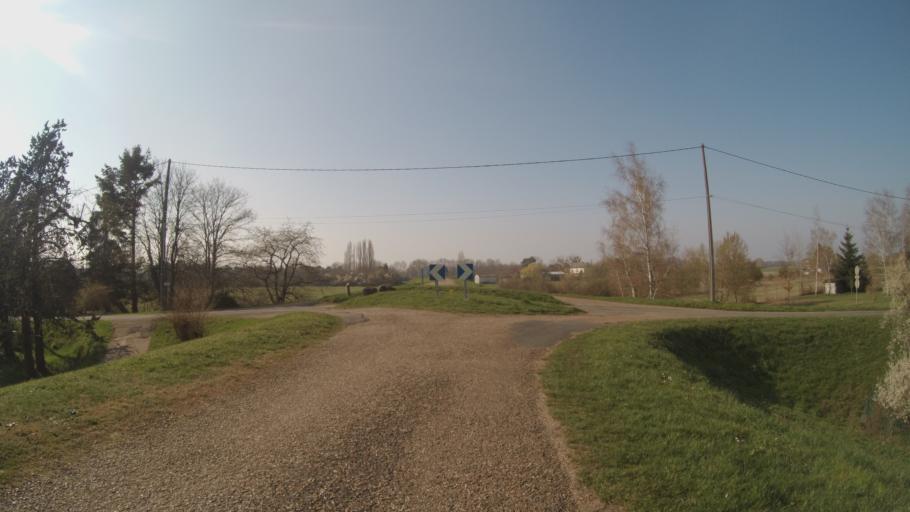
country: FR
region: Centre
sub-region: Departement du Loiret
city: Sandillon
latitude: 47.8657
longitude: 2.0402
